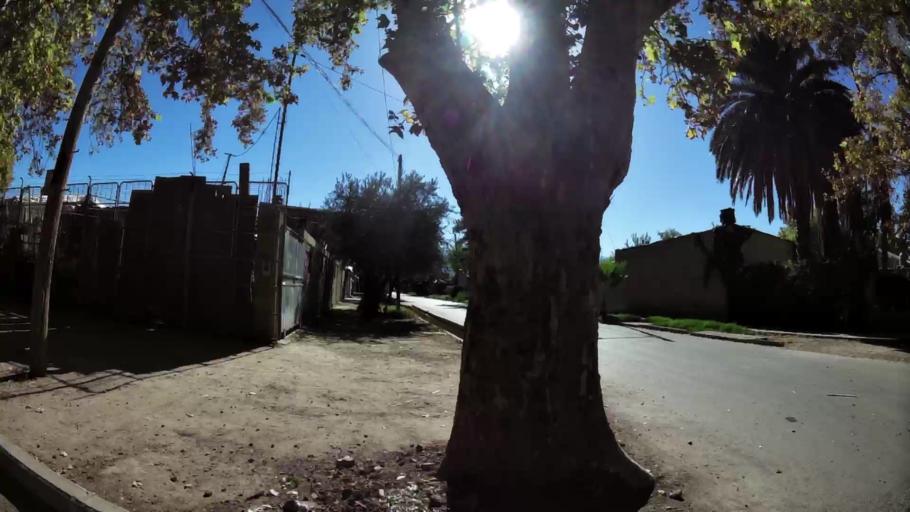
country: AR
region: Mendoza
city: Las Heras
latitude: -32.8379
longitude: -68.8251
